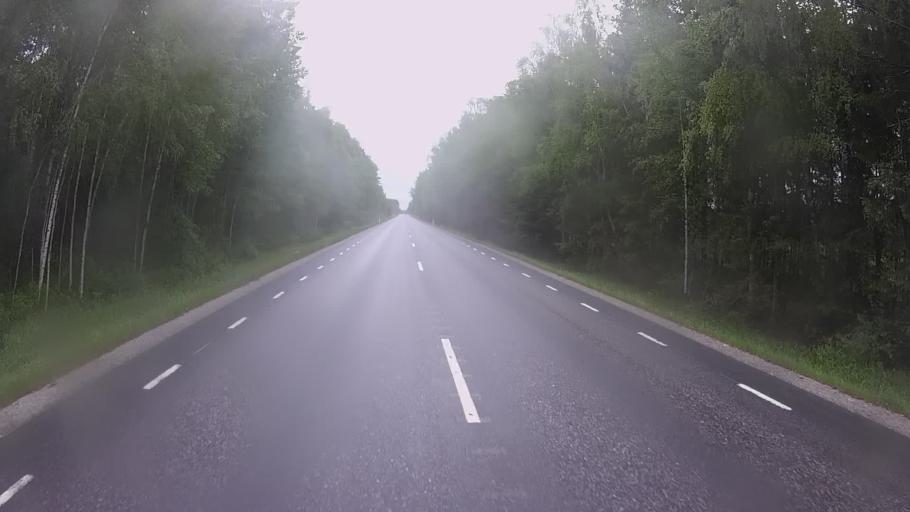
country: EE
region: Raplamaa
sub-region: Maerjamaa vald
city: Marjamaa
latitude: 58.9443
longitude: 24.5764
